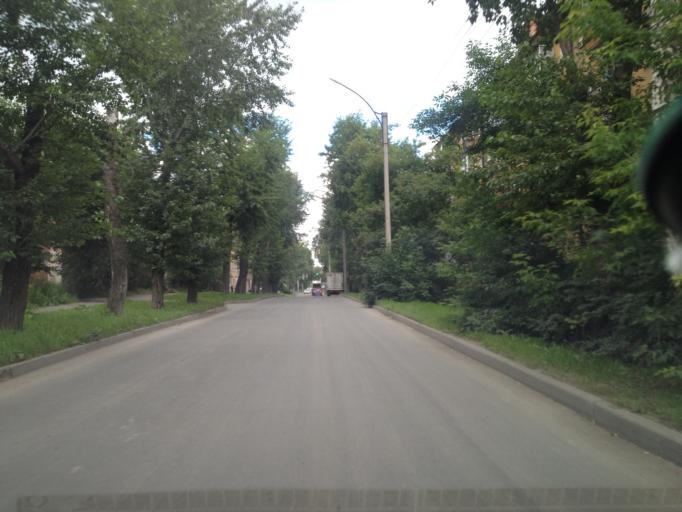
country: RU
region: Sverdlovsk
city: Shuvakish
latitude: 56.8691
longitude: 60.5271
